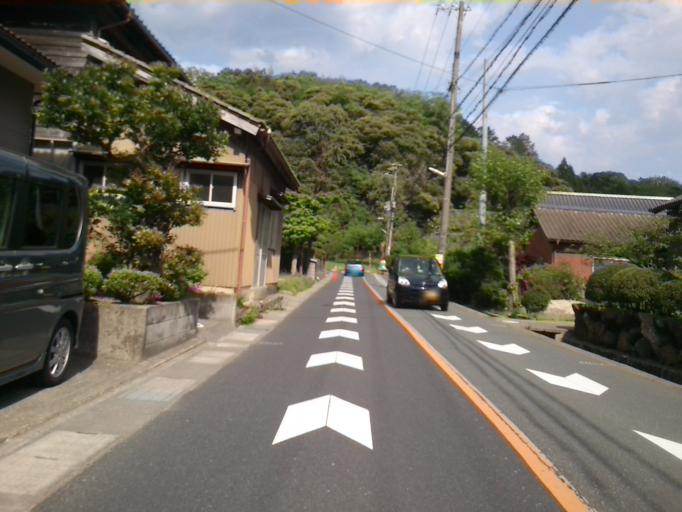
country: JP
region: Kyoto
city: Miyazu
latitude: 35.6814
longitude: 135.0554
